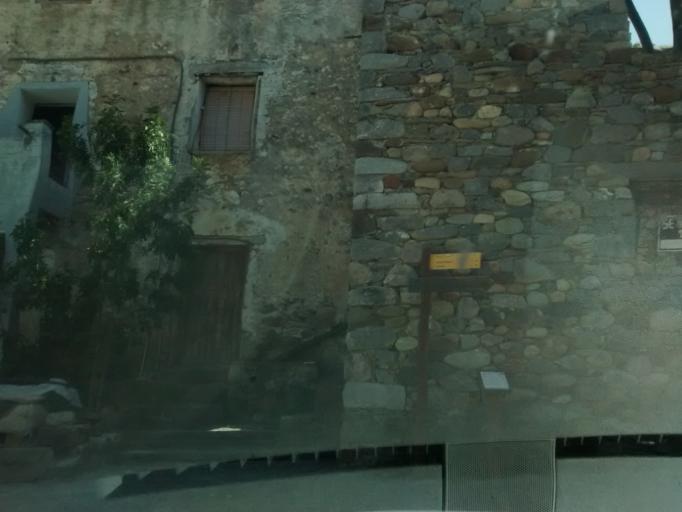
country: ES
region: Aragon
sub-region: Provincia de Huesca
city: Laspuna
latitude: 42.5410
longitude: 0.1955
